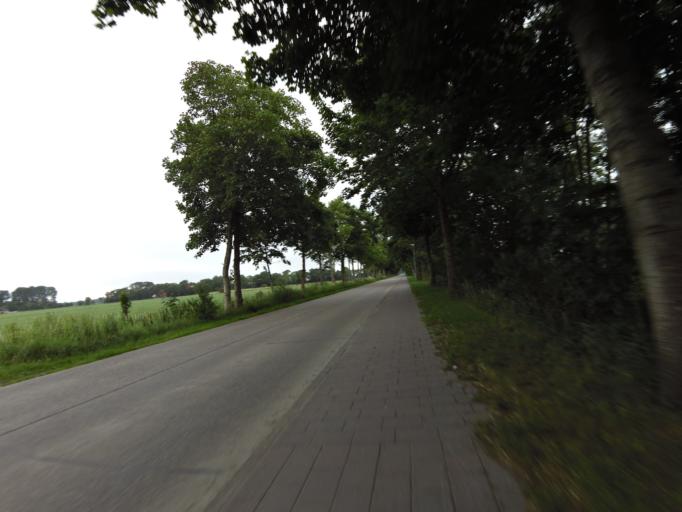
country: DE
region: Lower Saxony
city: Padingbuttel
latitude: 53.7272
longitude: 8.5334
